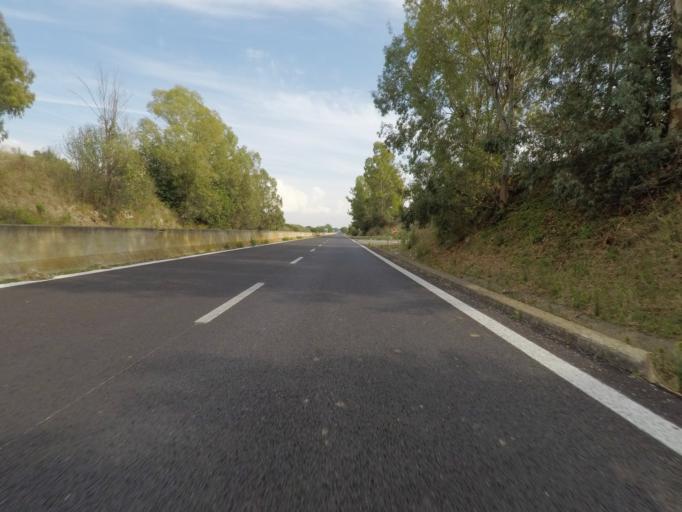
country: IT
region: Latium
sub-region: Provincia di Viterbo
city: Pescia Romana
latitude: 42.3989
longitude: 11.5114
